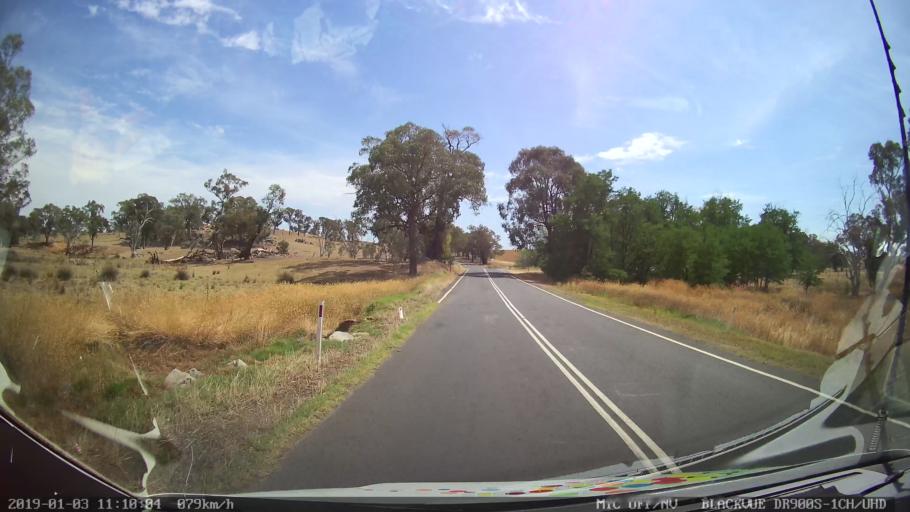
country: AU
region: New South Wales
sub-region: Young
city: Young
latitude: -34.2309
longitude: 148.2571
